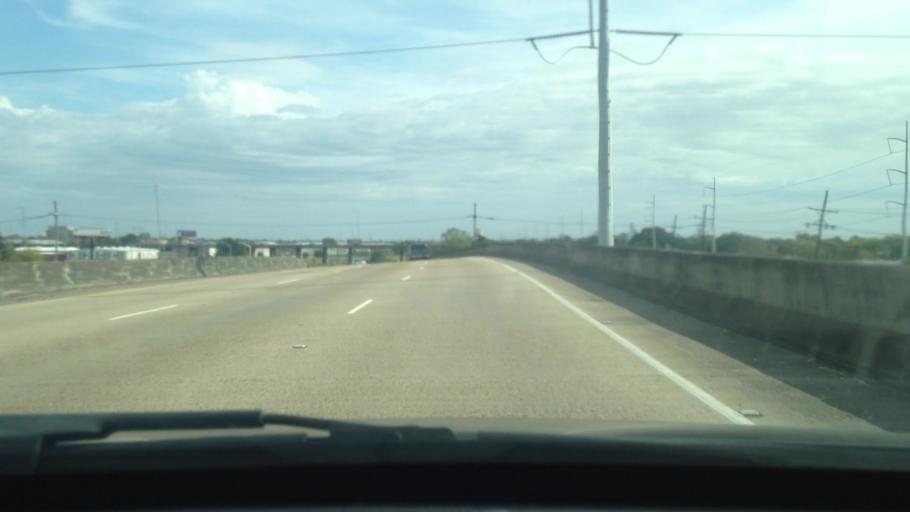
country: US
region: Louisiana
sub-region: Jefferson Parish
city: Metairie Terrace
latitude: 29.9708
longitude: -90.1625
